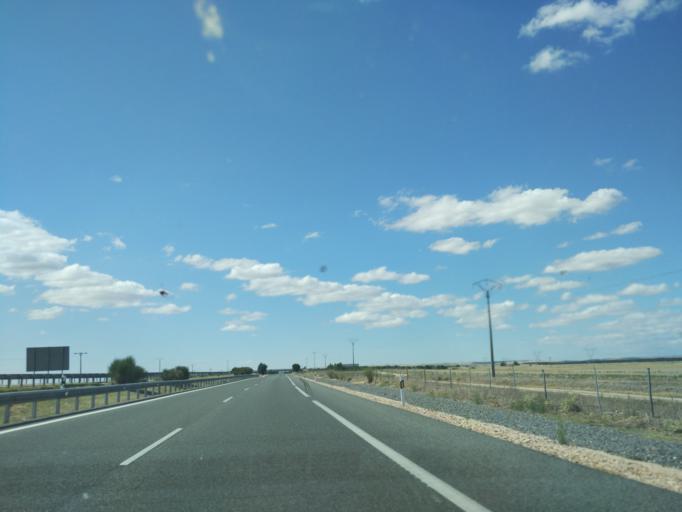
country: ES
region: Castille and Leon
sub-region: Provincia de Valladolid
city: San Vicente del Palacio
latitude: 41.2441
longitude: -4.8660
